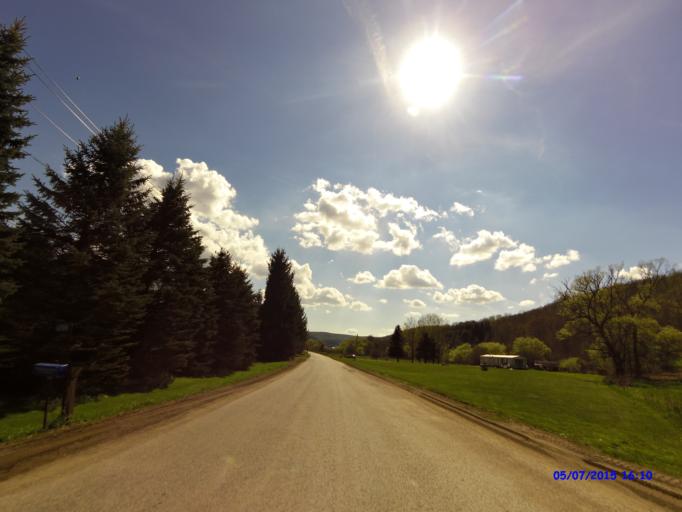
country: US
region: New York
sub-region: Cattaraugus County
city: Salamanca
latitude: 42.2700
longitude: -78.6224
